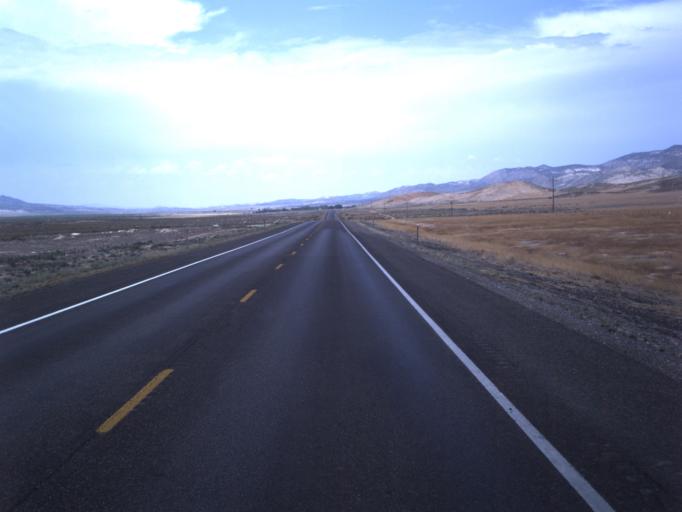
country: US
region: Utah
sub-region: Sanpete County
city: Gunnison
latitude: 39.1811
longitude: -111.8394
